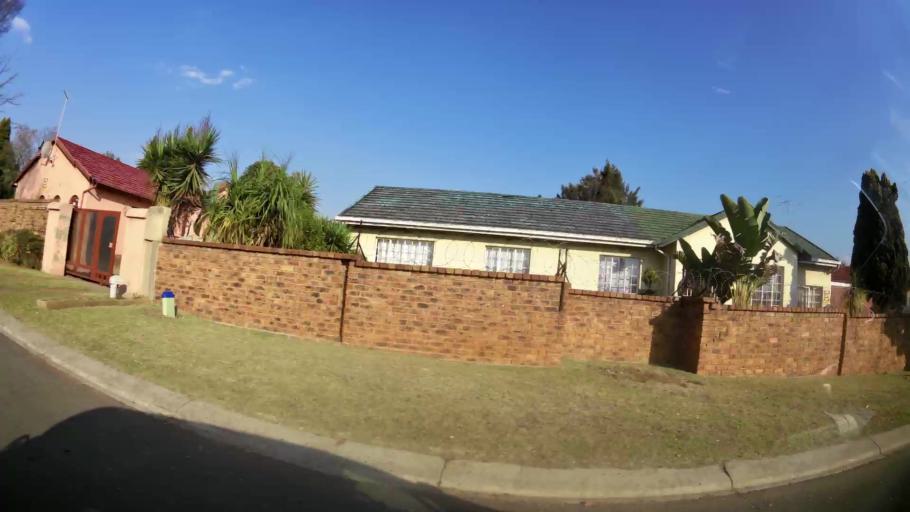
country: ZA
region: Gauteng
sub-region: Ekurhuleni Metropolitan Municipality
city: Benoni
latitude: -26.1350
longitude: 28.3652
